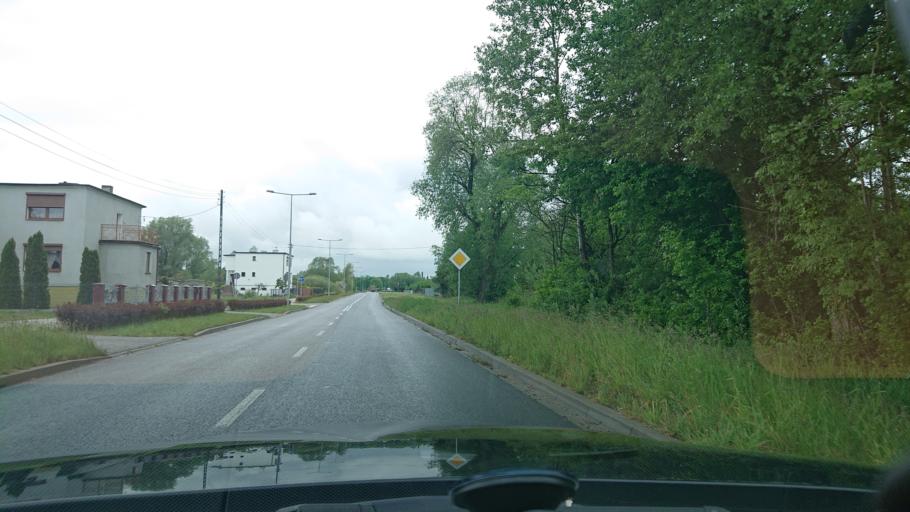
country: PL
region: Greater Poland Voivodeship
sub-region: Powiat gnieznienski
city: Gniezno
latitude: 52.5223
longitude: 17.6208
